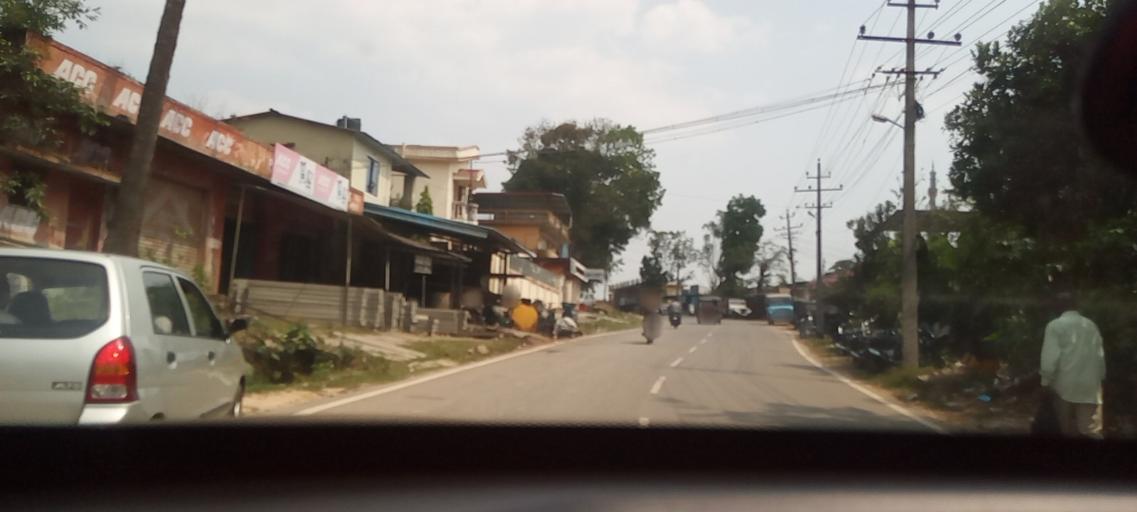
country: IN
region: Karnataka
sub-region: Chikmagalur
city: Mudigere
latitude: 13.2435
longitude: 75.6479
